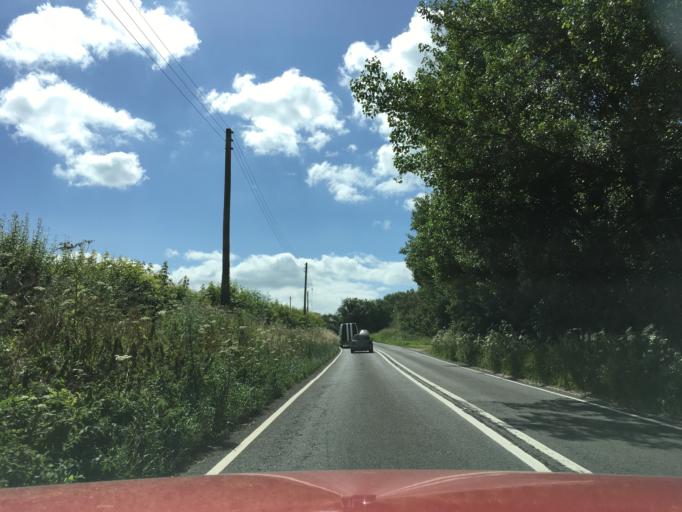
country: GB
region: England
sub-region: Buckinghamshire
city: Winslow
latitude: 51.8977
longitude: -0.8317
